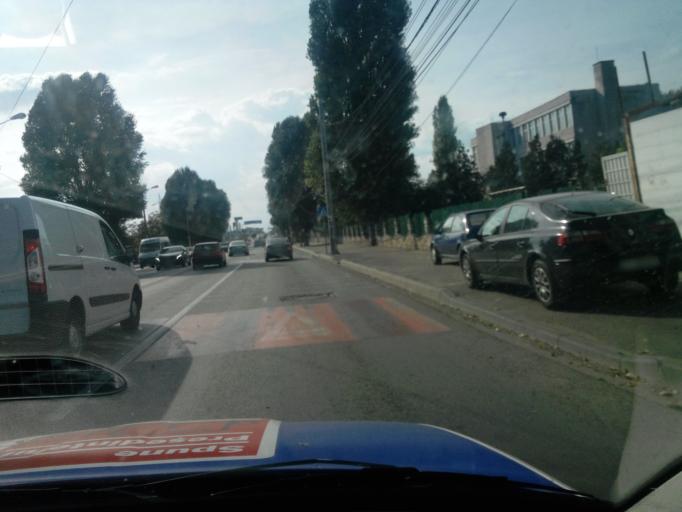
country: RO
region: Constanta
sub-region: Municipiul Constanta
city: Constanta
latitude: 44.1398
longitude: 28.6215
